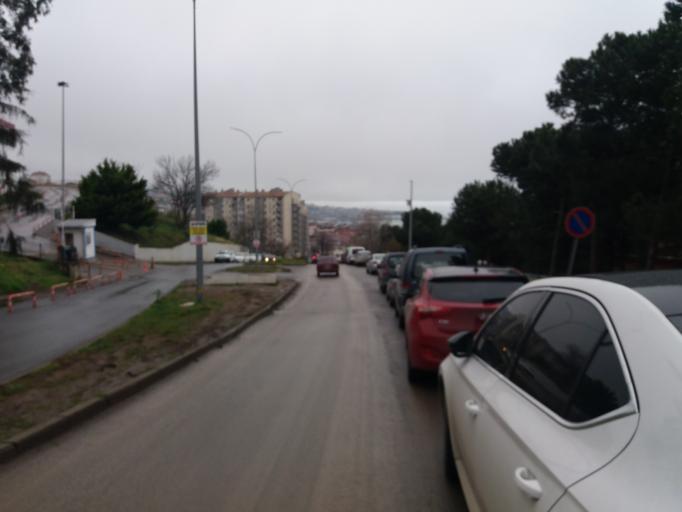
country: TR
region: Trabzon
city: Trabzon
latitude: 40.9937
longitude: 39.7696
